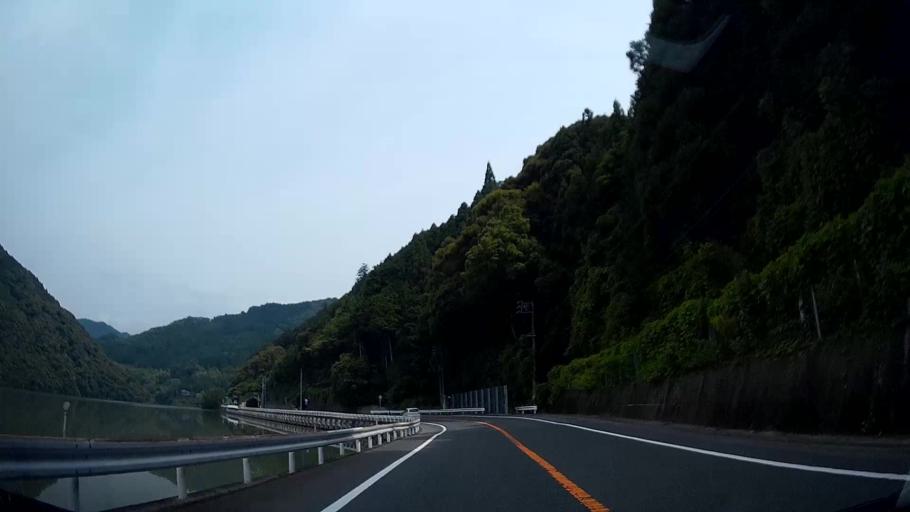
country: JP
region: Shizuoka
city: Hamakita
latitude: 34.8970
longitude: 137.8137
